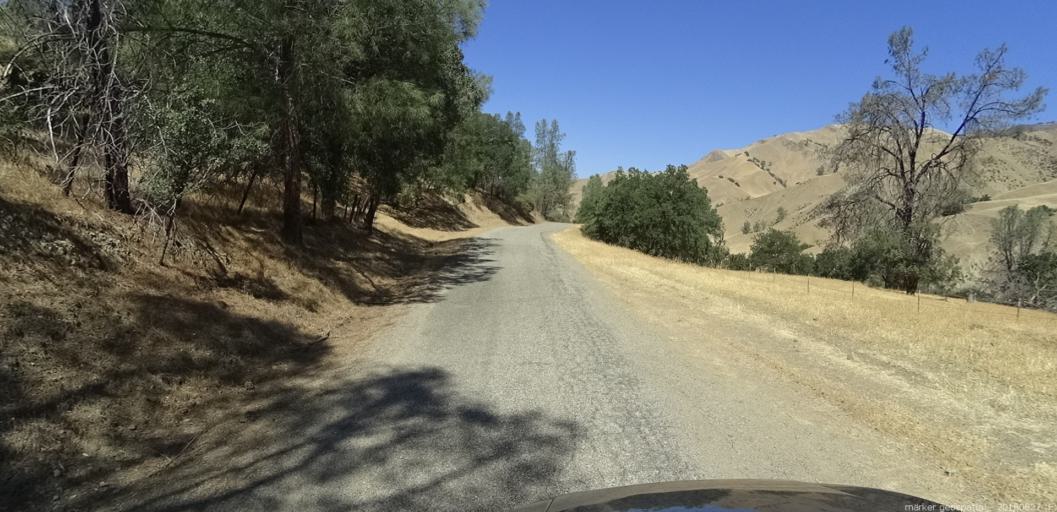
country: US
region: California
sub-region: Monterey County
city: King City
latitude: 36.2897
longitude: -120.8640
